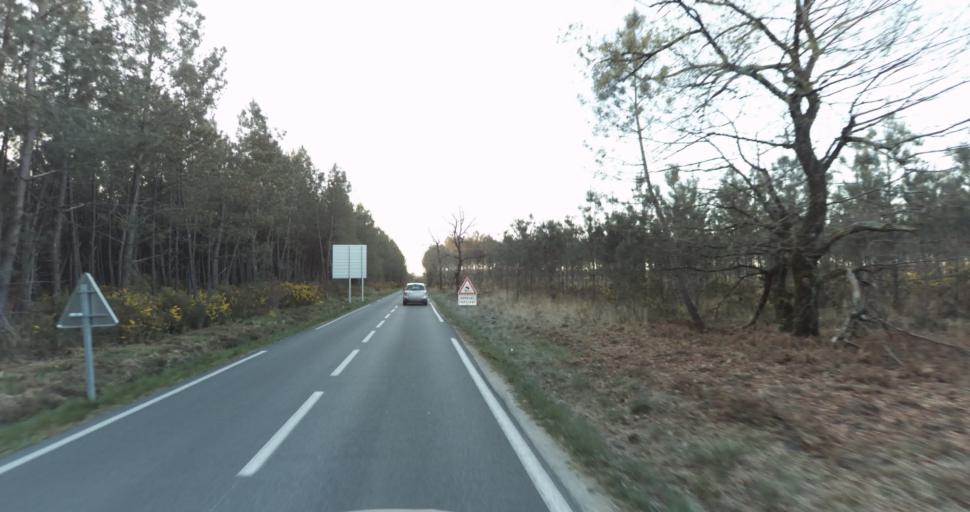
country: FR
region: Aquitaine
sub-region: Departement de la Gironde
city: Martignas-sur-Jalle
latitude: 44.8307
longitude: -0.7670
